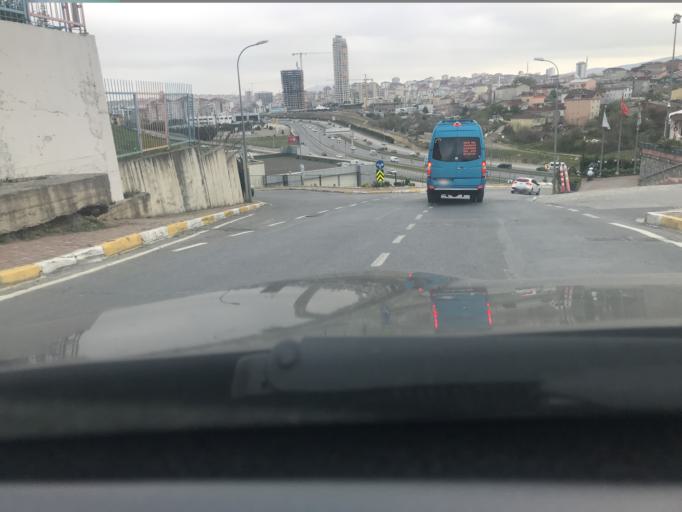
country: TR
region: Istanbul
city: Umraniye
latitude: 41.0368
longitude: 29.1606
